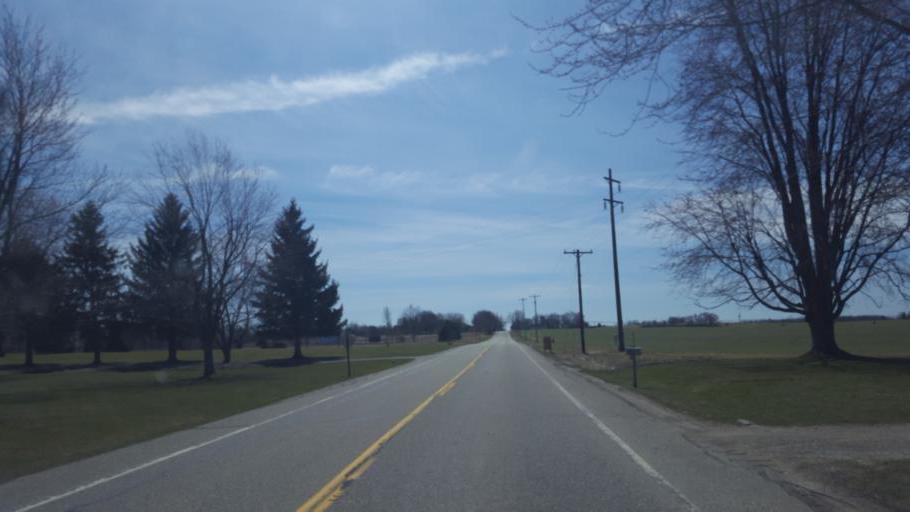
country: US
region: Michigan
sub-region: Montcalm County
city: Edmore
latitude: 43.4640
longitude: -85.0443
